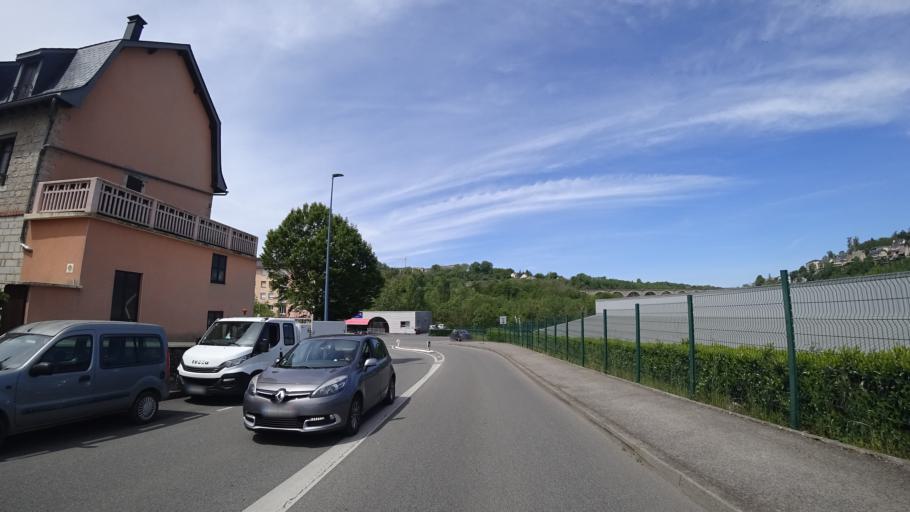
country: FR
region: Midi-Pyrenees
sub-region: Departement de l'Aveyron
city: Rodez
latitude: 44.3449
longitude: 2.5654
